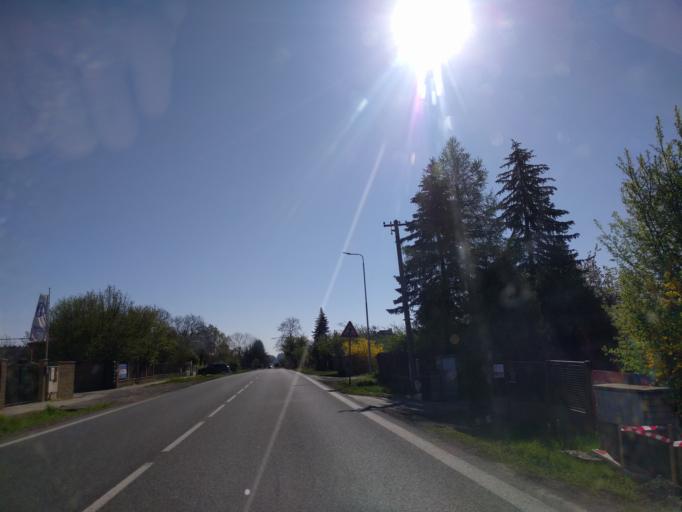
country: CZ
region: Central Bohemia
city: Mukarov
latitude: 49.9896
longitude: 14.7473
